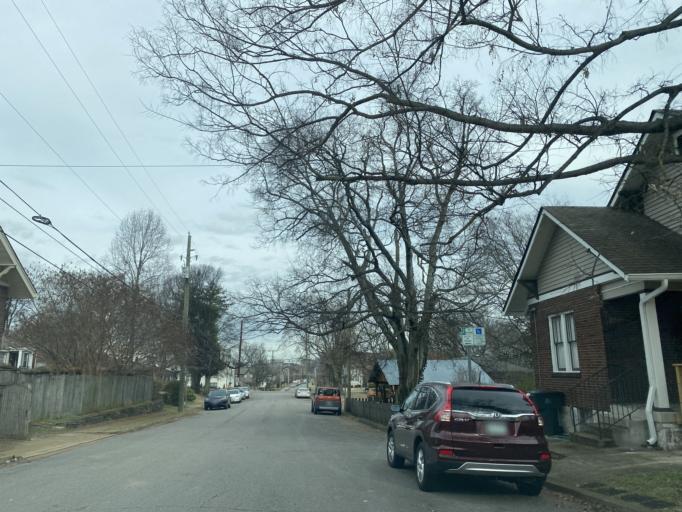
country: US
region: Tennessee
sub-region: Davidson County
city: Nashville
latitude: 36.1347
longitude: -86.7908
